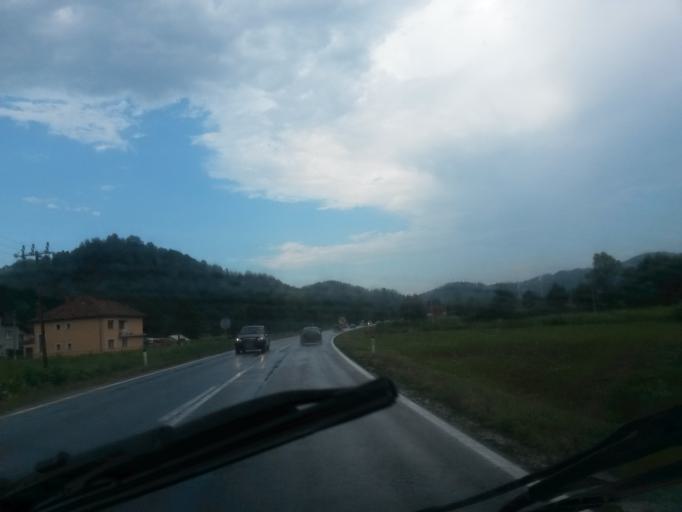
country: BA
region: Federation of Bosnia and Herzegovina
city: Lijesnica
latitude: 44.5140
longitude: 18.0813
